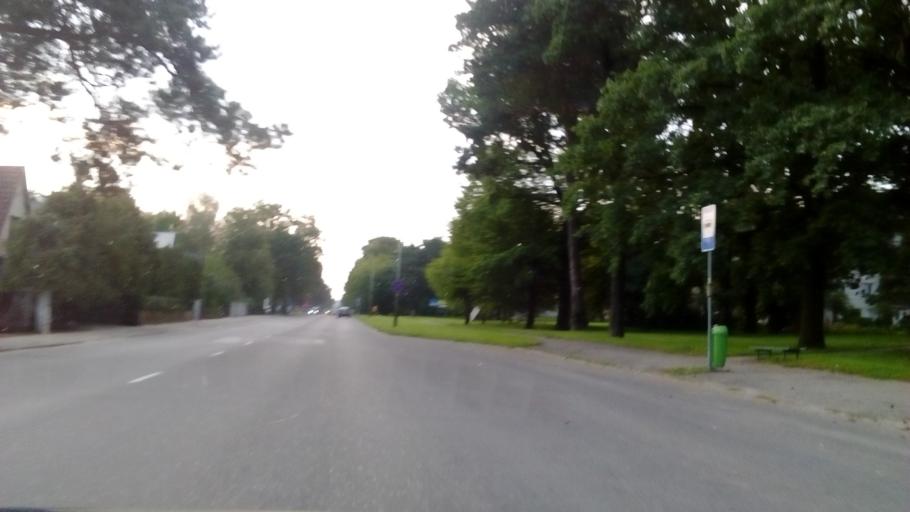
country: LT
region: Alytaus apskritis
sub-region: Alytus
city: Alytus
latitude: 54.3860
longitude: 24.0451
